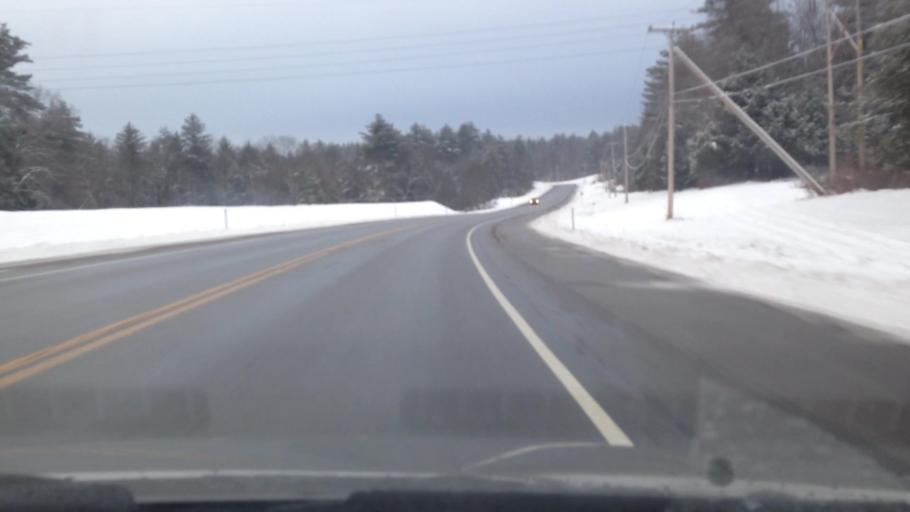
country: US
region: New Hampshire
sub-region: Cheshire County
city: Keene
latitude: 42.9738
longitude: -72.2581
